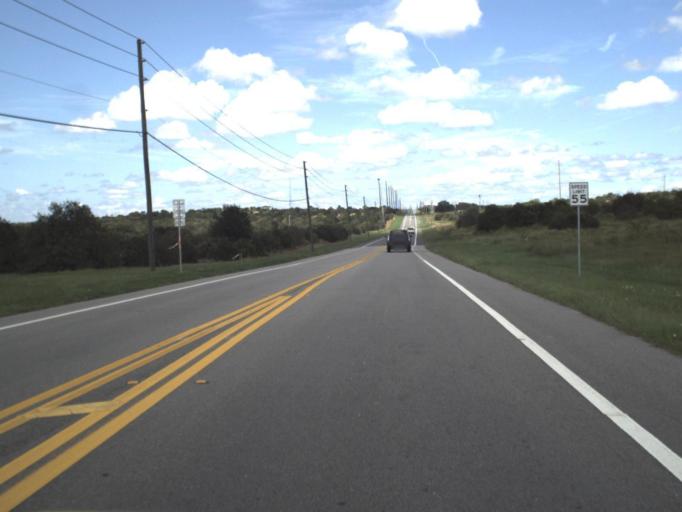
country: US
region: Florida
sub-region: Polk County
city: Dundee
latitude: 27.9784
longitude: -81.5948
